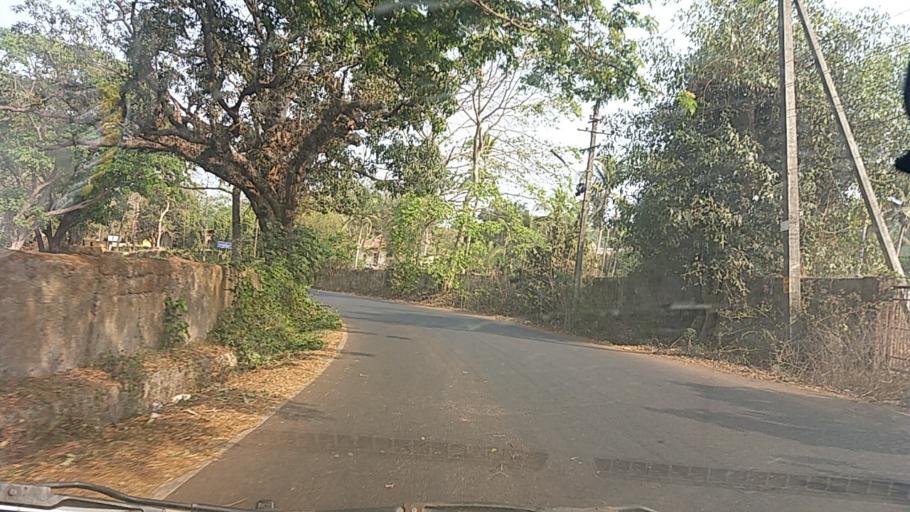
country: IN
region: Goa
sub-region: North Goa
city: Jua
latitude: 15.4939
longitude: 73.9180
